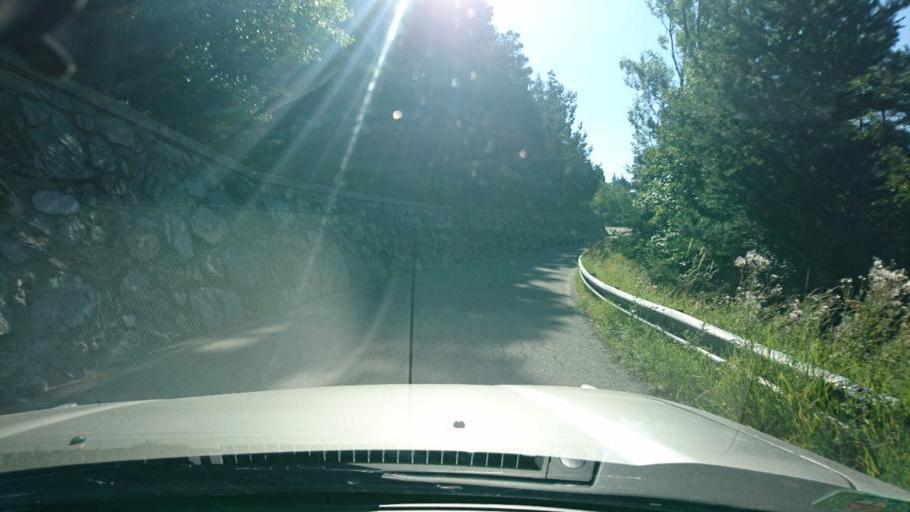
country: IT
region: Aosta Valley
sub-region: Valle d'Aosta
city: Villeneuve
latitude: 45.7326
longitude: 7.2032
